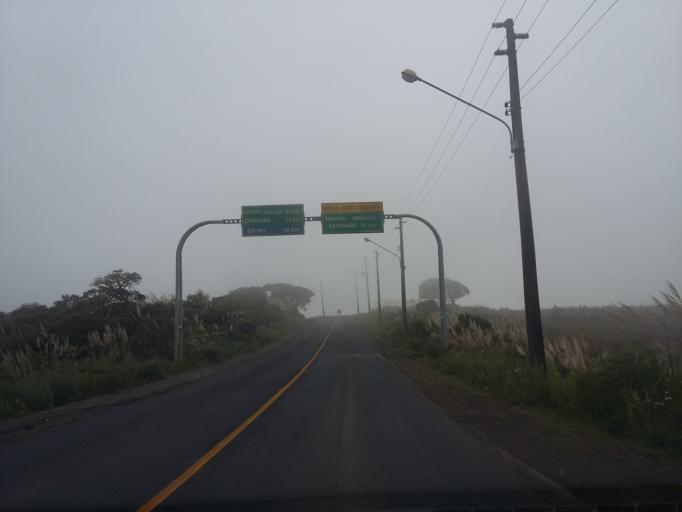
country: BR
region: Santa Catarina
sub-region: Lauro Muller
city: Lauro Muller
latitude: -28.3959
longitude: -49.5507
